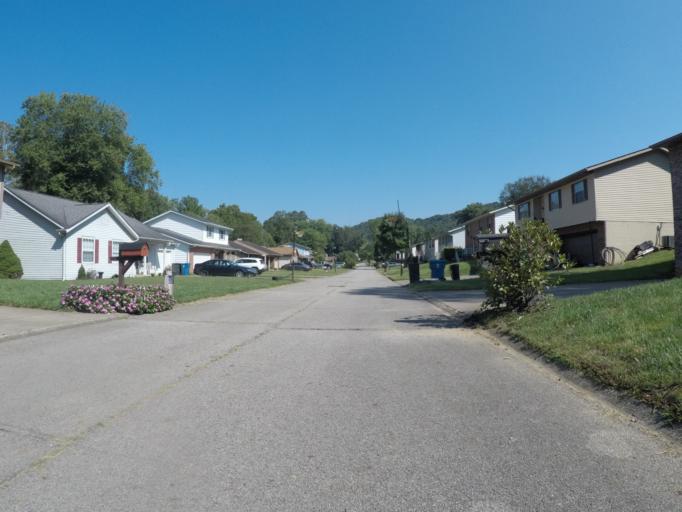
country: US
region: West Virginia
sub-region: Cabell County
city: Barboursville
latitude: 38.3669
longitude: -82.2762
